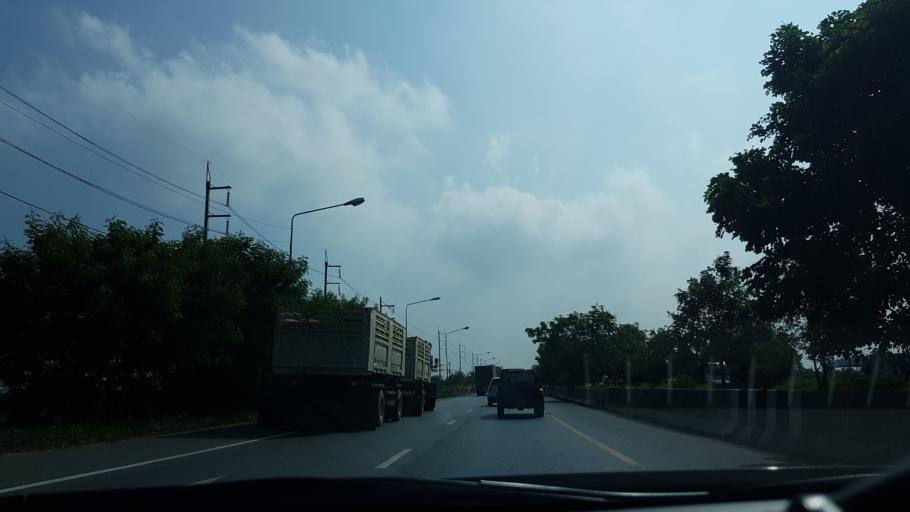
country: TH
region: Phra Nakhon Si Ayutthaya
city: Bang Pa-in
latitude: 14.1692
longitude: 100.5929
